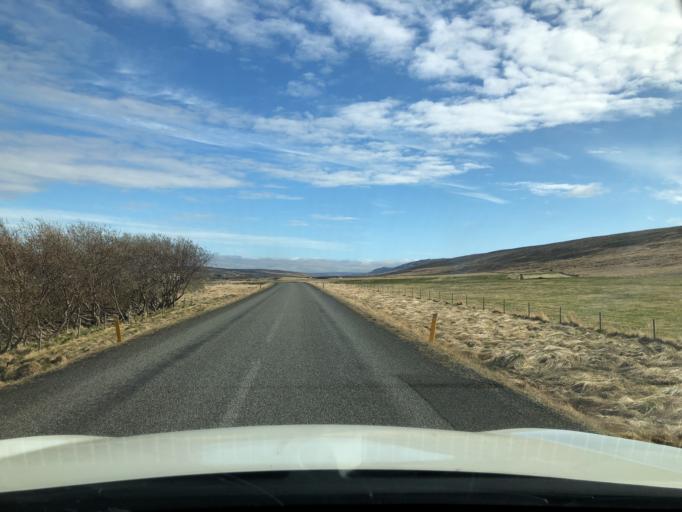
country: IS
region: West
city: Borgarnes
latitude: 65.0947
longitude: -21.7243
